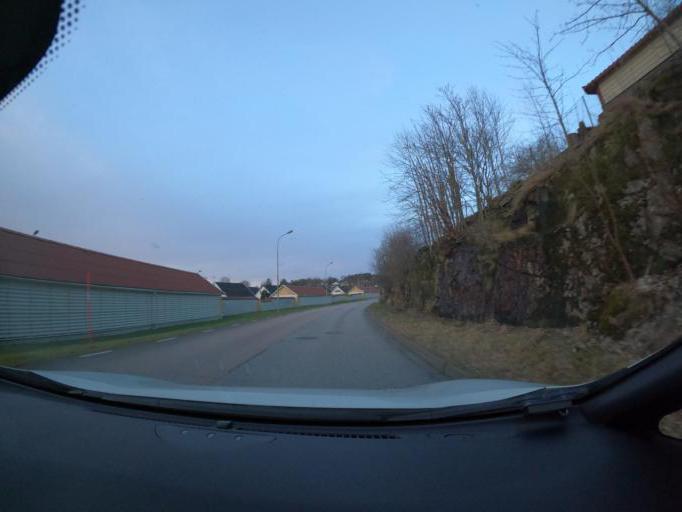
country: SE
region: Vaestra Goetaland
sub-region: Harryda Kommun
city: Molnlycke
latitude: 57.6459
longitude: 12.1211
